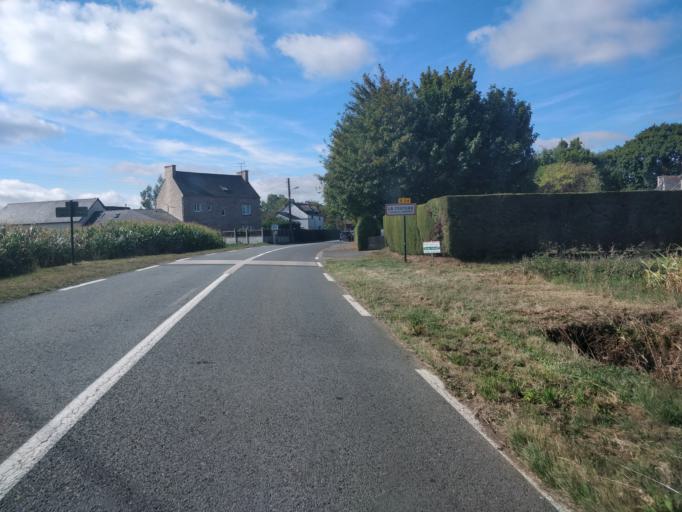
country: FR
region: Brittany
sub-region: Departement des Cotes-d'Armor
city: Erquy
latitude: 48.5989
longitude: -2.4722
